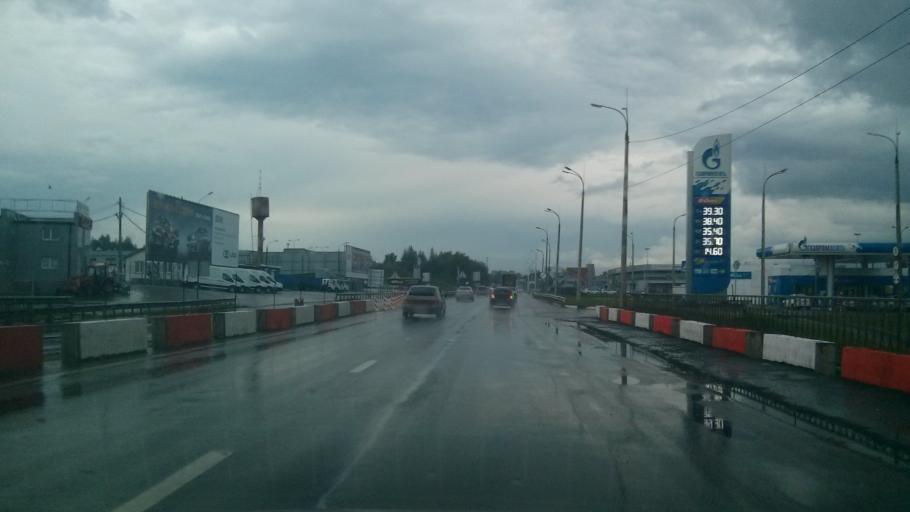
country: RU
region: Nizjnij Novgorod
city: Afonino
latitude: 56.2357
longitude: 44.0234
